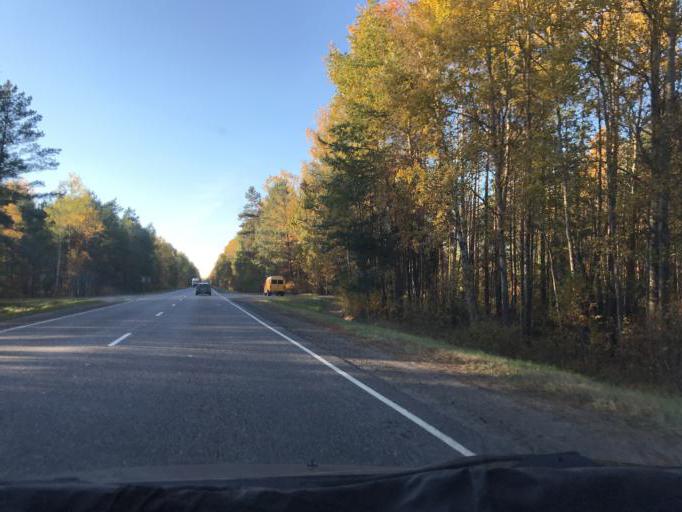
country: BY
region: Gomel
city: Pyetrykaw
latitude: 52.2493
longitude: 28.3697
